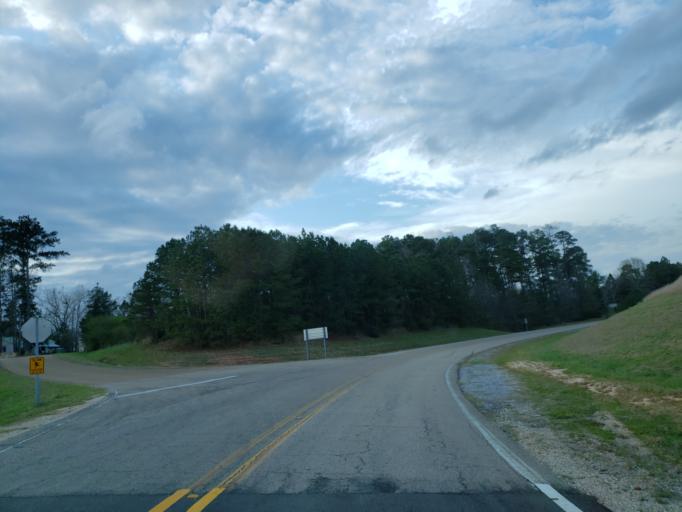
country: US
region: Mississippi
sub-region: Clarke County
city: Stonewall
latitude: 32.2133
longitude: -88.6989
